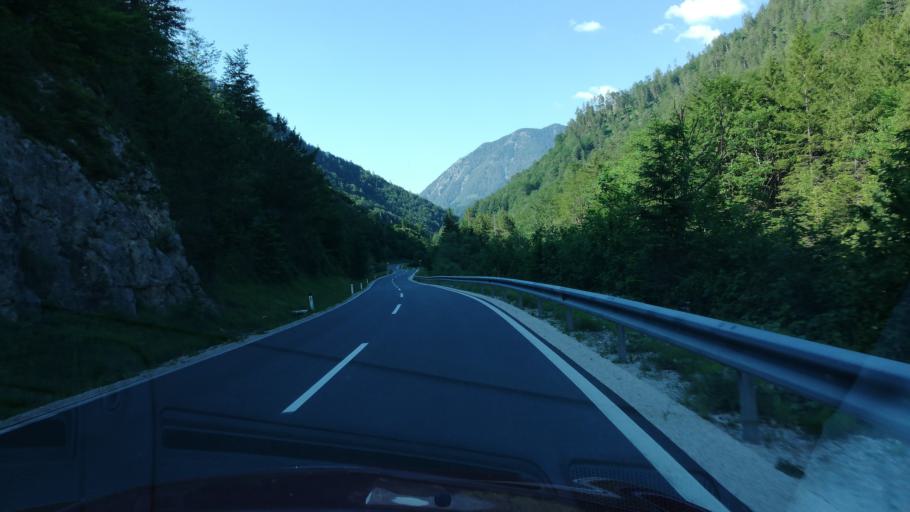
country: AT
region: Upper Austria
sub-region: Politischer Bezirk Kirchdorf an der Krems
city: Rossleithen
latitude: 47.7515
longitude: 14.1624
